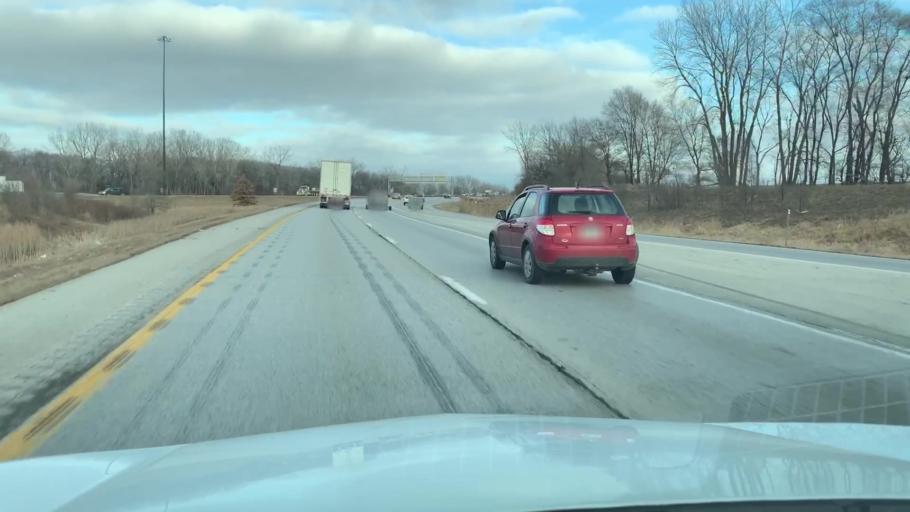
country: US
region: Iowa
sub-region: Polk County
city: Des Moines
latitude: 41.6520
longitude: -93.5720
